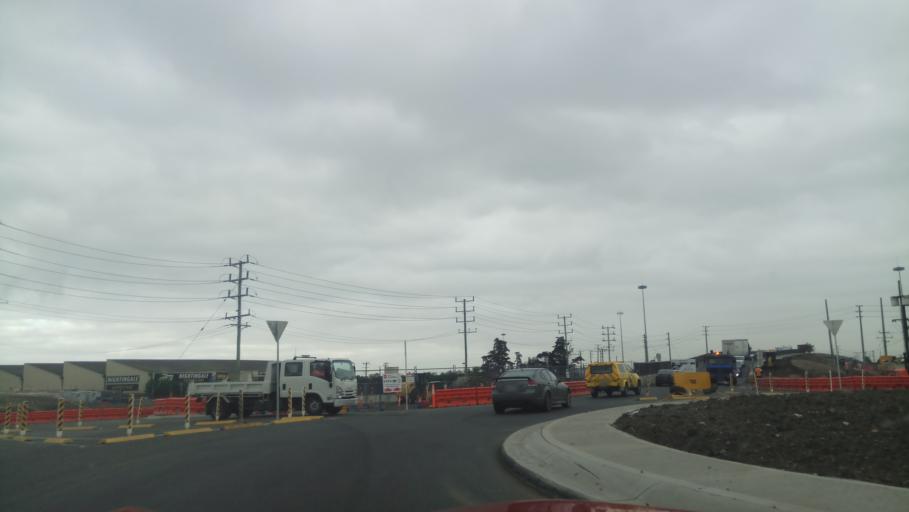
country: AU
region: Victoria
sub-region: Brimbank
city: Brooklyn
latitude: -37.8310
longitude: 144.8177
